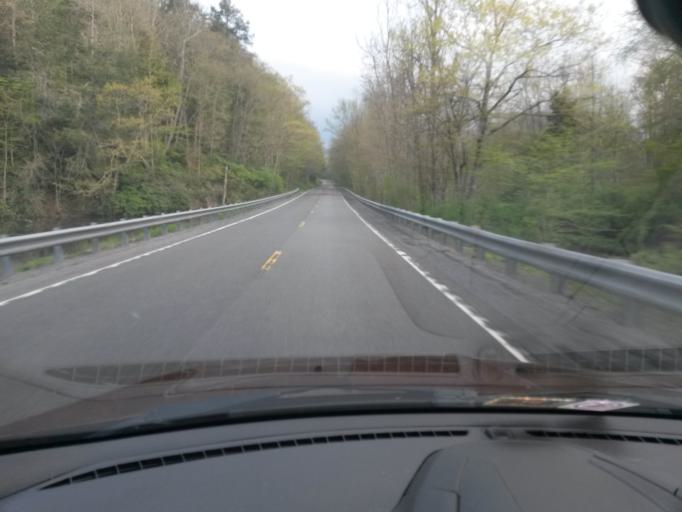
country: US
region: Virginia
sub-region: Highland County
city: Monterey
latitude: 38.5495
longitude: -79.7308
